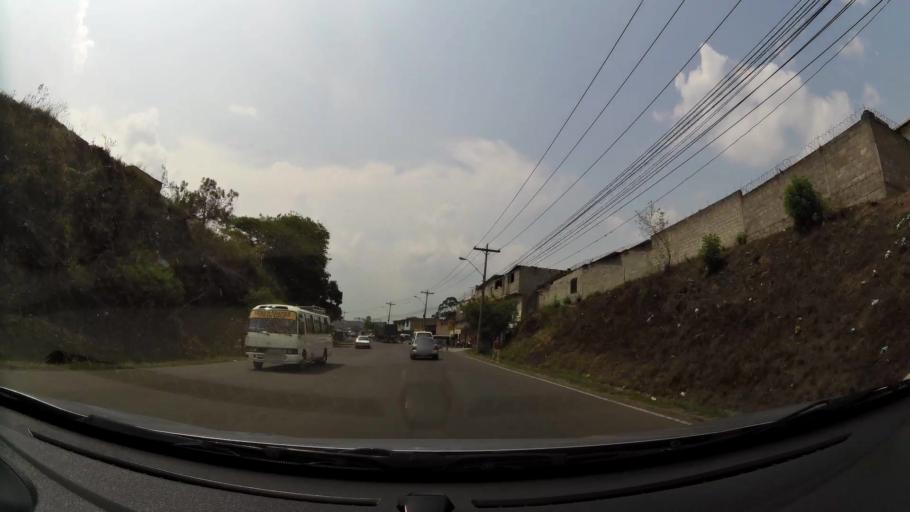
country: HN
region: Francisco Morazan
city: Tegucigalpa
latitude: 14.1173
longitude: -87.2230
